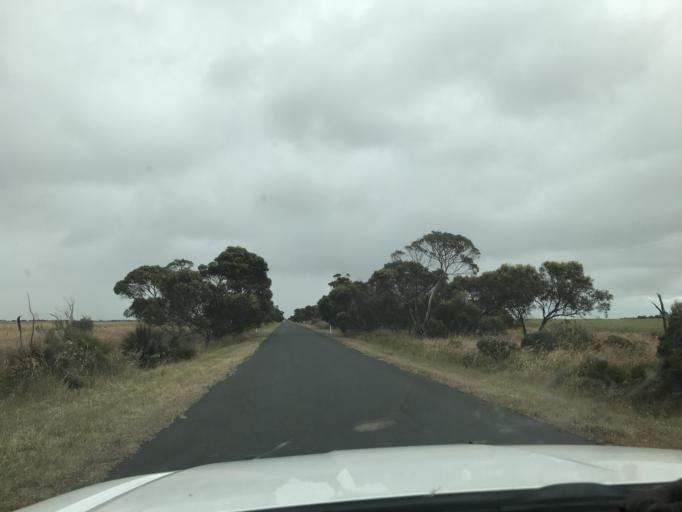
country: AU
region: South Australia
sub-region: Tatiara
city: Bordertown
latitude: -36.1186
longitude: 141.0492
